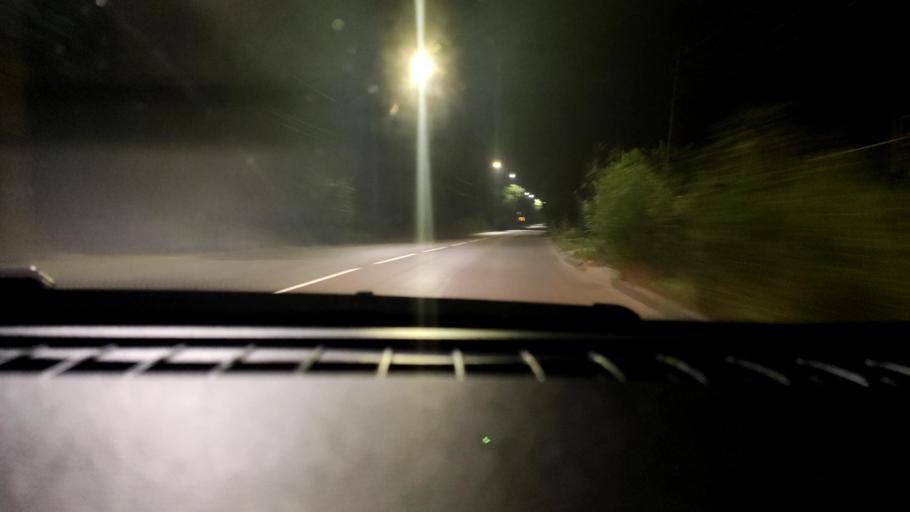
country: RU
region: Voronezj
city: Voronezh
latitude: 51.7326
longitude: 39.2604
